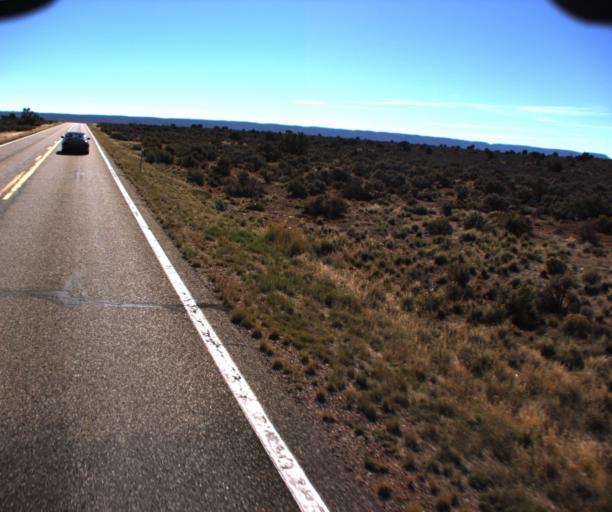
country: US
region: Arizona
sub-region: Coconino County
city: Fredonia
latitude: 36.8873
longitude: -112.3486
